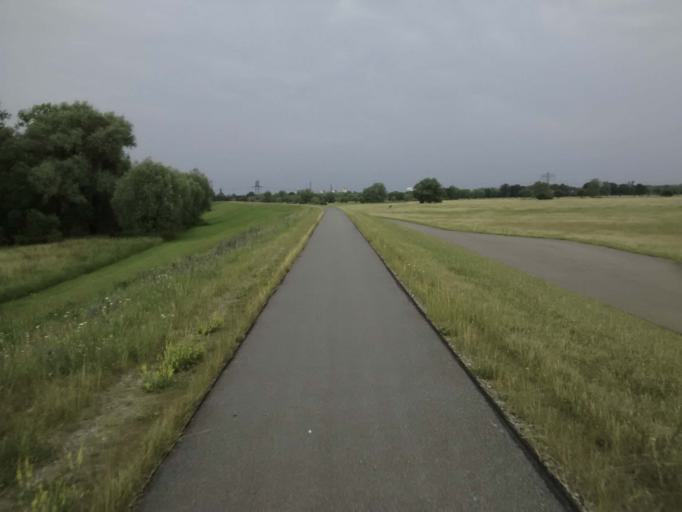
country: DE
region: Brandenburg
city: Breese
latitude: 52.9704
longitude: 11.7867
